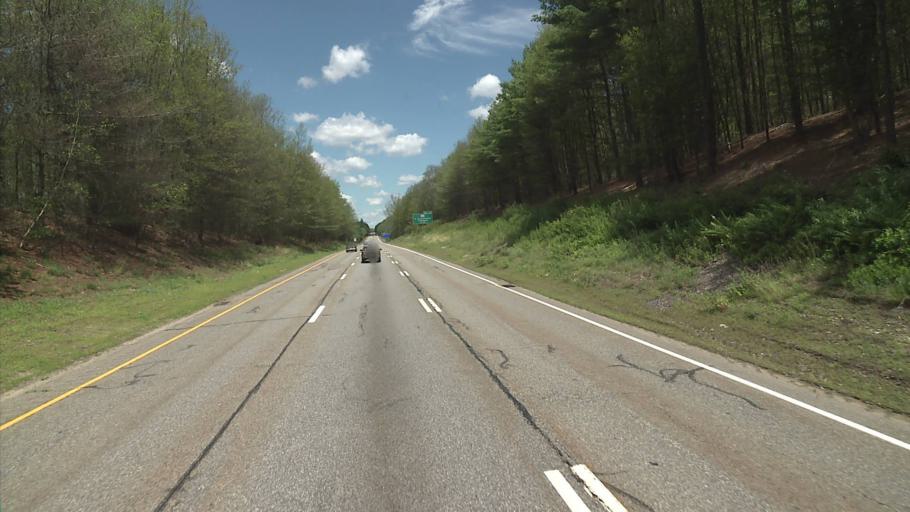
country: US
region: Connecticut
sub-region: Windham County
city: Thompson
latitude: 41.9535
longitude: -71.8795
